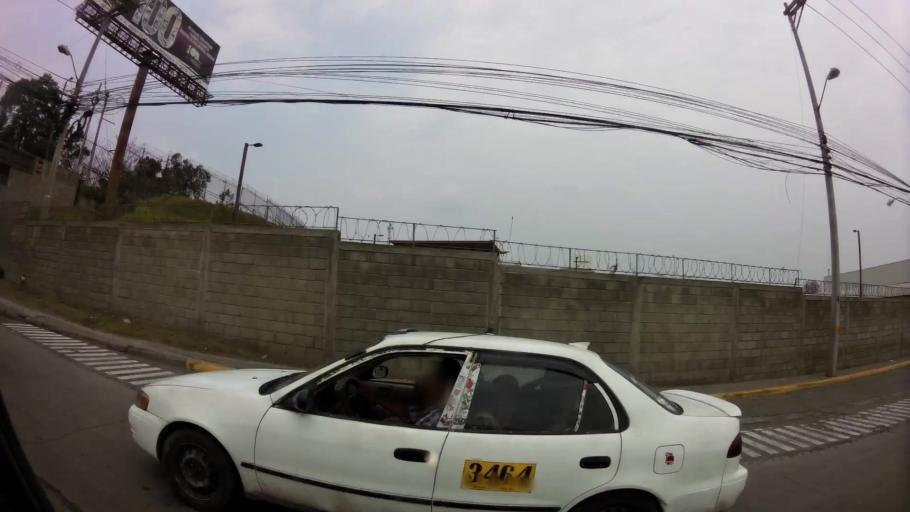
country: HN
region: Francisco Morazan
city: Tegucigalpa
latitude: 14.0756
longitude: -87.2112
